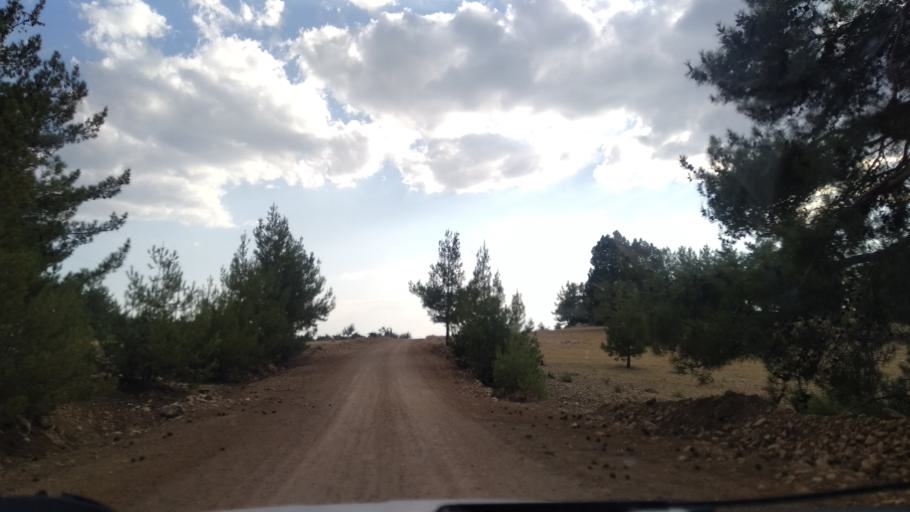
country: TR
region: Mersin
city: Sarikavak
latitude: 36.5940
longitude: 33.6831
